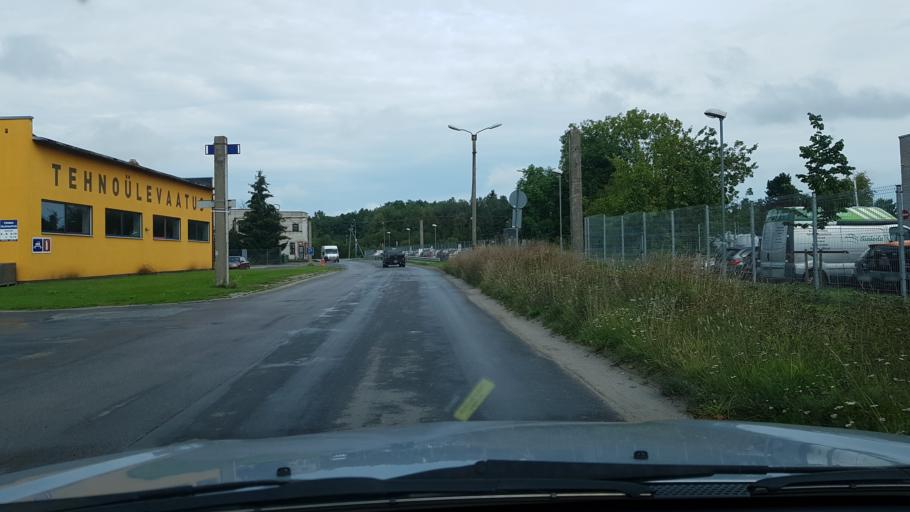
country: EE
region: Harju
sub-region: Rae vald
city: Jueri
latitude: 59.3582
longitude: 24.9286
